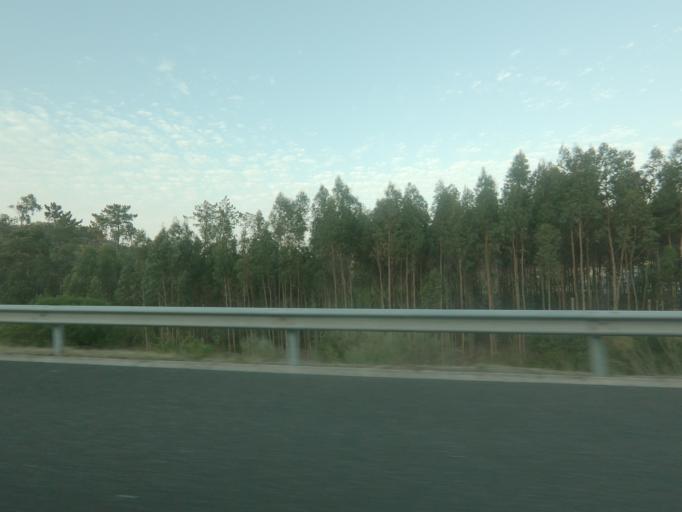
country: PT
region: Leiria
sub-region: Leiria
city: Caranguejeira
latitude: 39.7223
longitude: -8.7148
